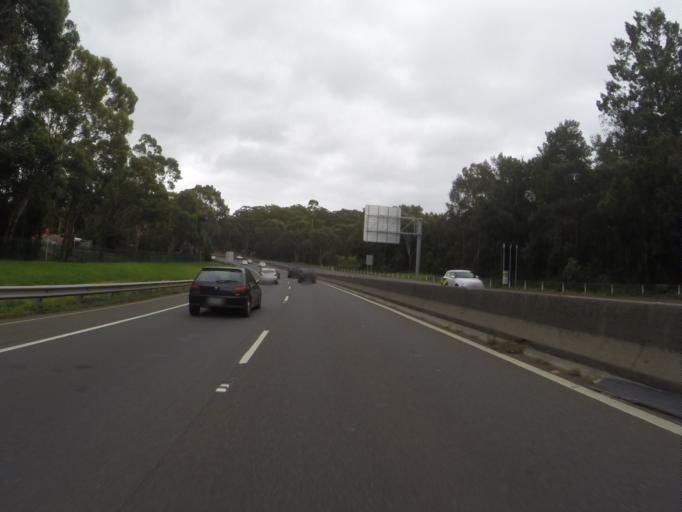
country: AU
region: New South Wales
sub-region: Wollongong
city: Mount Ousley
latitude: -34.4052
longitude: 150.8837
